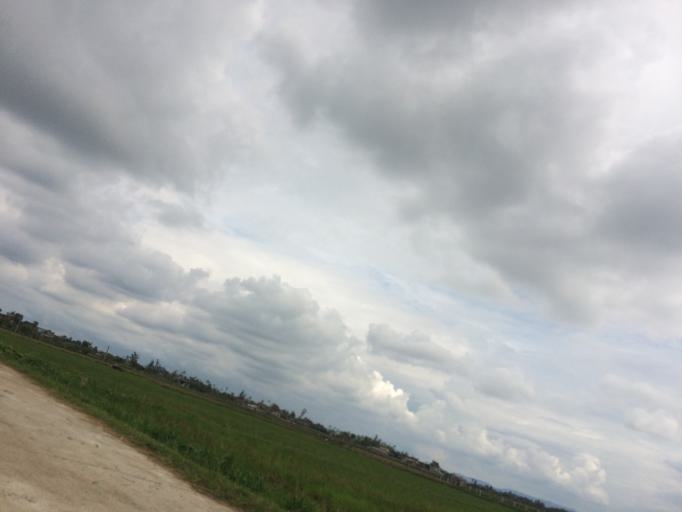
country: VN
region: Ha Tinh
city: Ha Tinh
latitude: 18.3414
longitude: 105.9284
